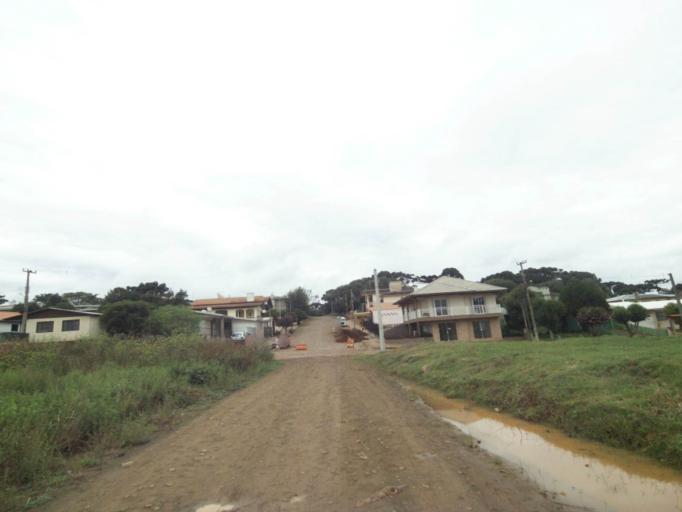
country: BR
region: Rio Grande do Sul
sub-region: Lagoa Vermelha
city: Lagoa Vermelha
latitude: -28.2167
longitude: -51.5239
